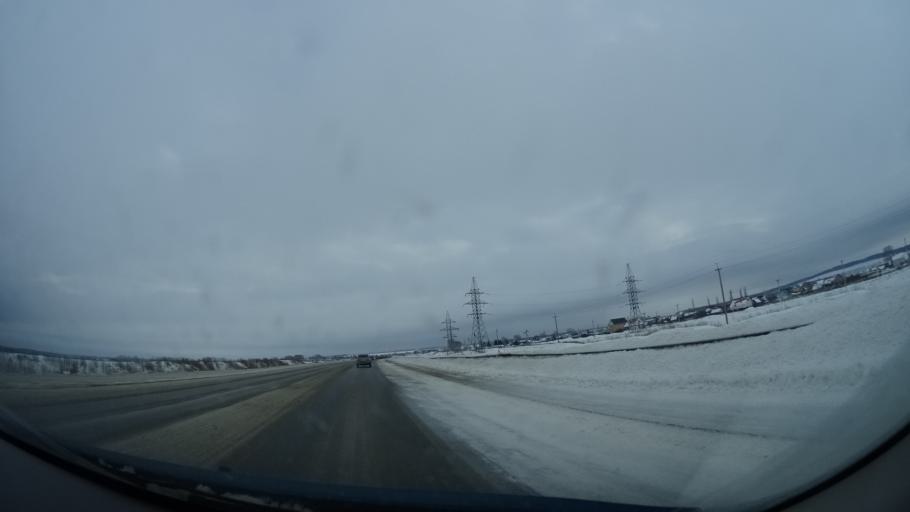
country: RU
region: Bashkortostan
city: Mikhaylovka
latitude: 54.8762
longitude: 55.7245
